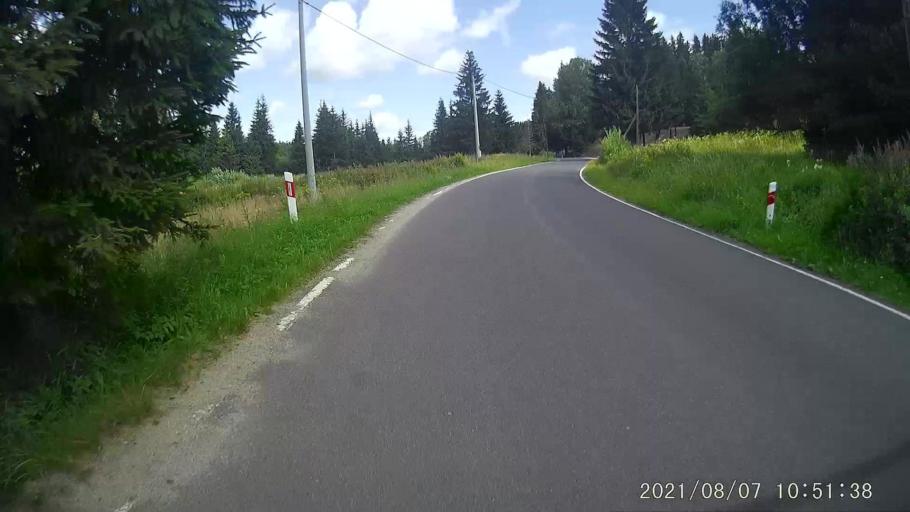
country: CZ
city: Rokytnice v Orlickych Horach
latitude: 50.2876
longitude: 16.4681
